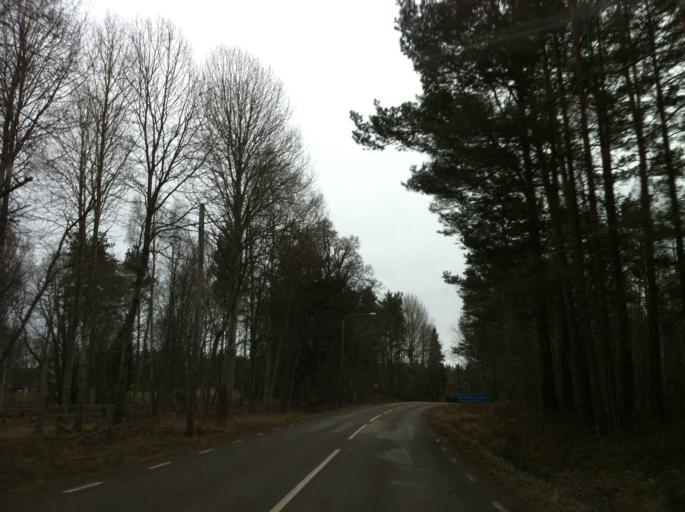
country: SE
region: Kalmar
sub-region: Vasterviks Kommun
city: Vaestervik
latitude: 57.8070
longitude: 16.5938
